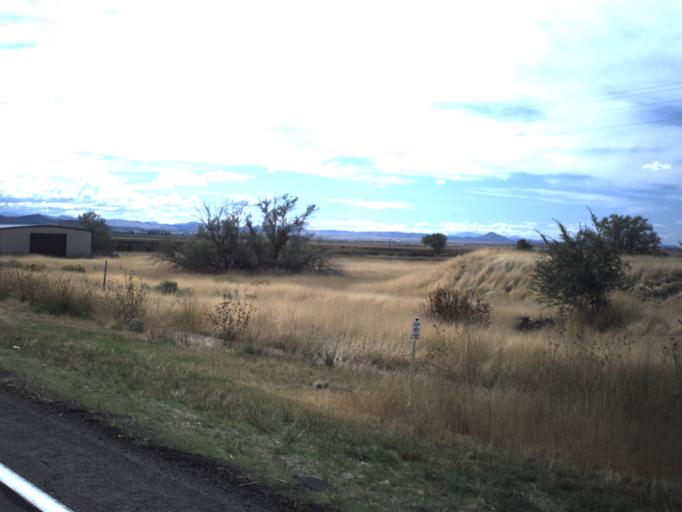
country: US
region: Utah
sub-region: Millard County
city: Fillmore
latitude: 38.8790
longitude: -112.4121
